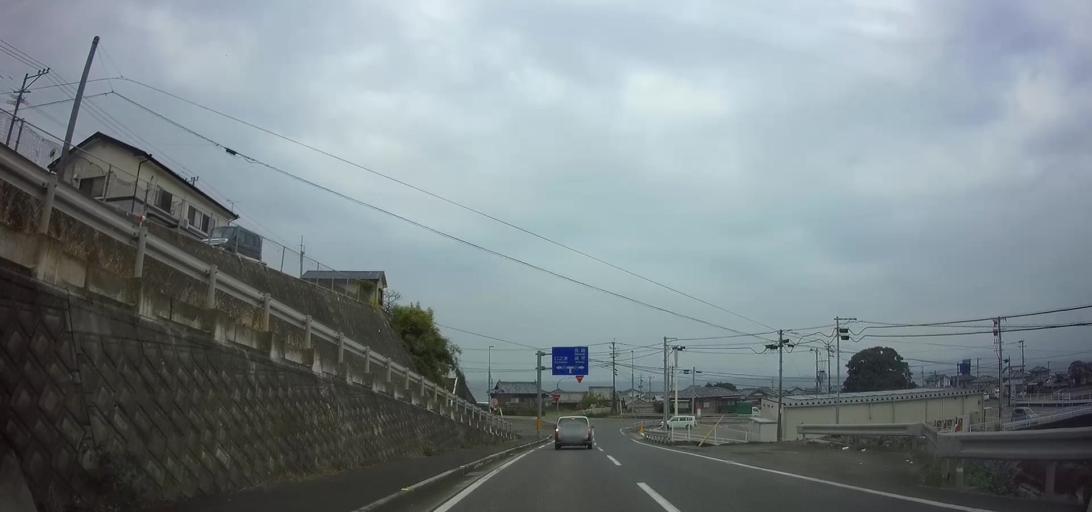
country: JP
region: Nagasaki
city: Shimabara
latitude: 32.7078
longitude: 130.1887
